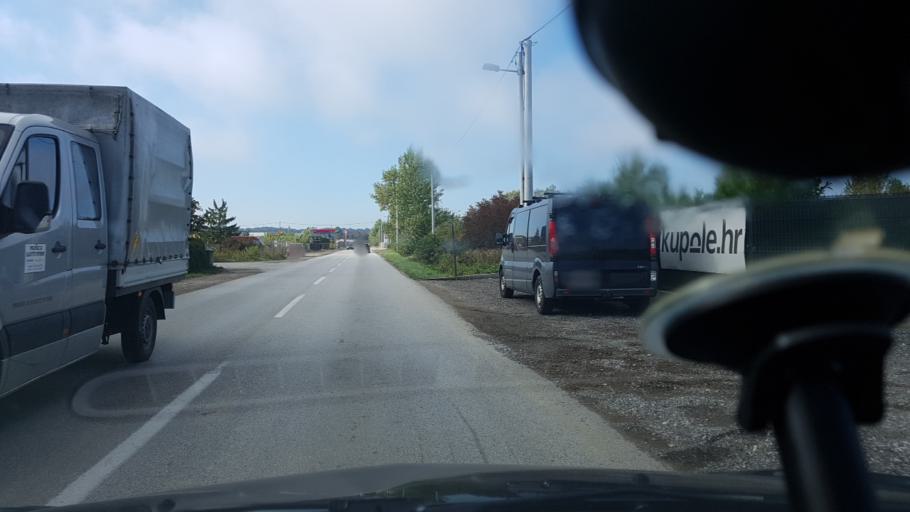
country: HR
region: Zagrebacka
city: Rakitje
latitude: 45.7805
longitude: 15.8299
